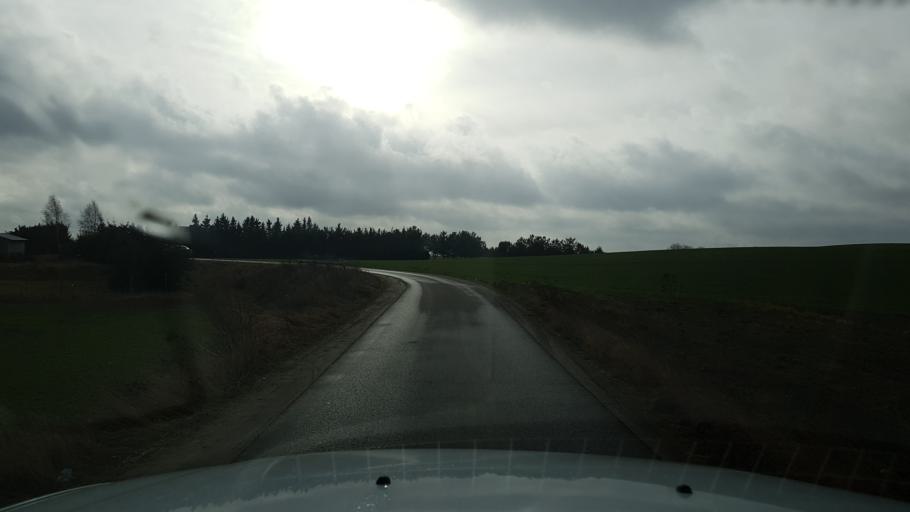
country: PL
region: West Pomeranian Voivodeship
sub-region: Powiat szczecinecki
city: Szczecinek
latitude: 53.7122
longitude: 16.7432
